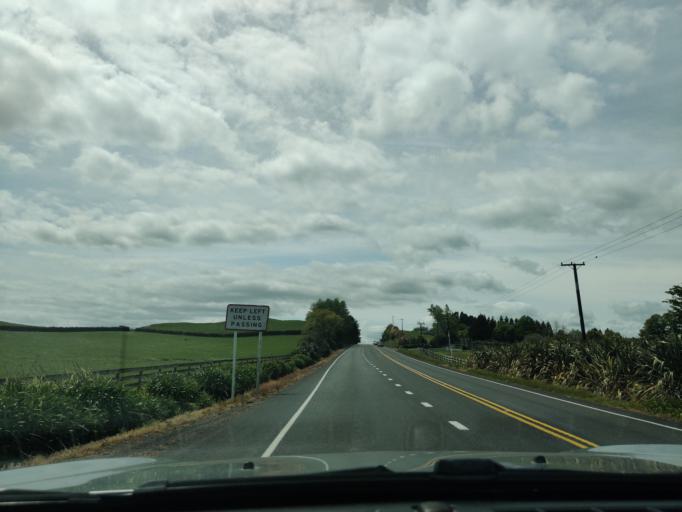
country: NZ
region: Taranaki
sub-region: New Plymouth District
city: New Plymouth
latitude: -39.1512
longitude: 174.1619
